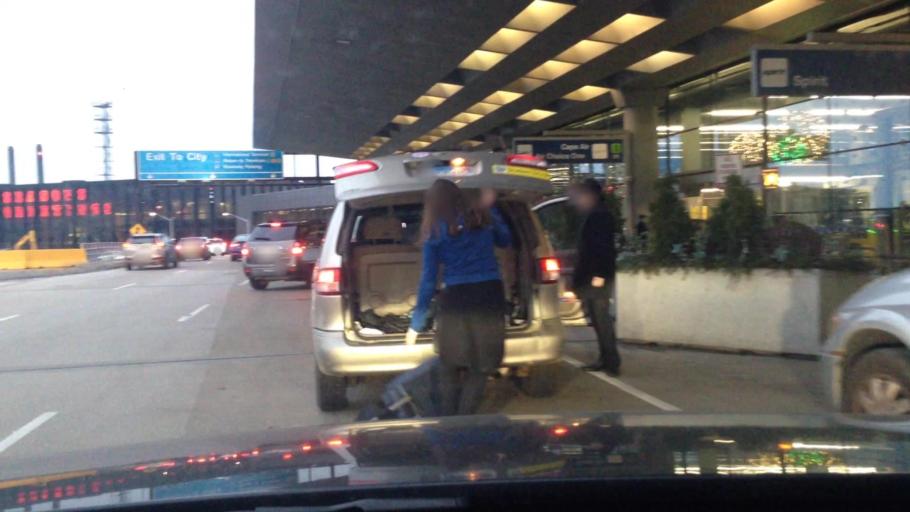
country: US
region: Illinois
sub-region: Cook County
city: Rosemont
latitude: 41.9777
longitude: -87.9002
